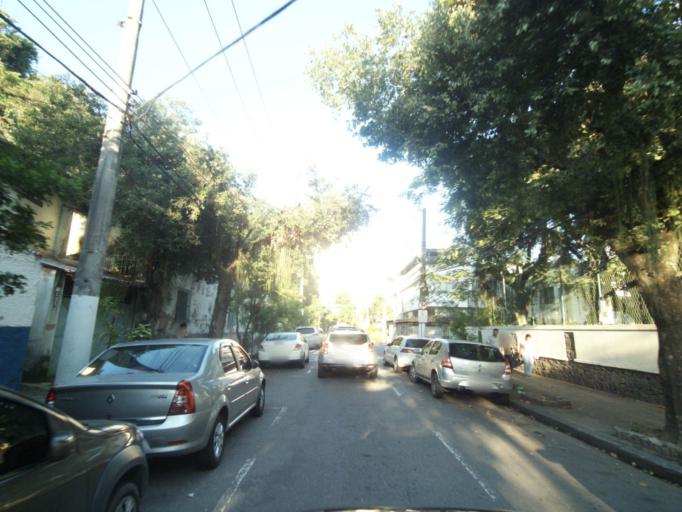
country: BR
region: Rio de Janeiro
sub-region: Niteroi
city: Niteroi
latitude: -22.8926
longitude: -43.1161
